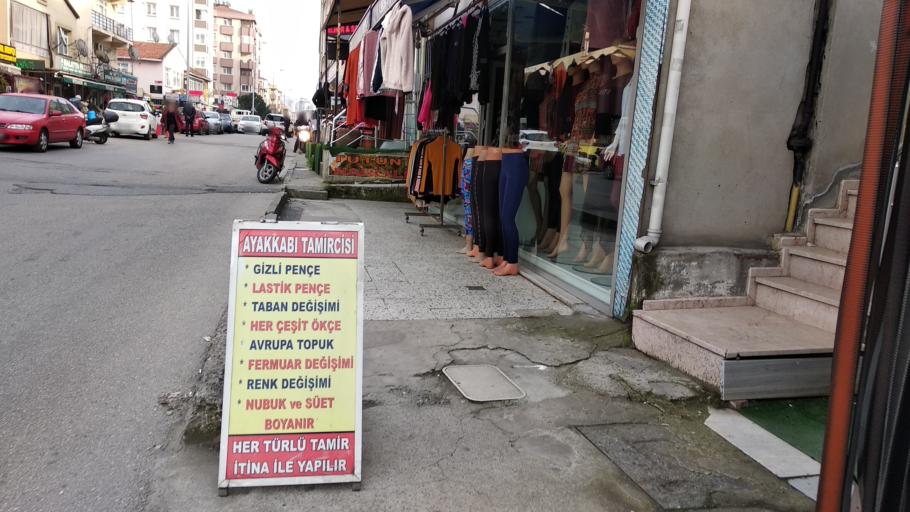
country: TR
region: Istanbul
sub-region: Atasehir
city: Atasehir
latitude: 40.9734
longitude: 29.1147
